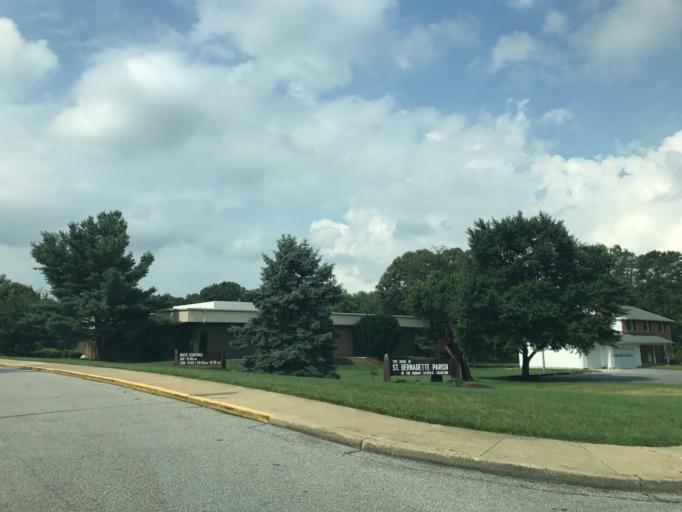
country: US
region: Maryland
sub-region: Anne Arundel County
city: South Gate
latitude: 39.1279
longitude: -76.6494
